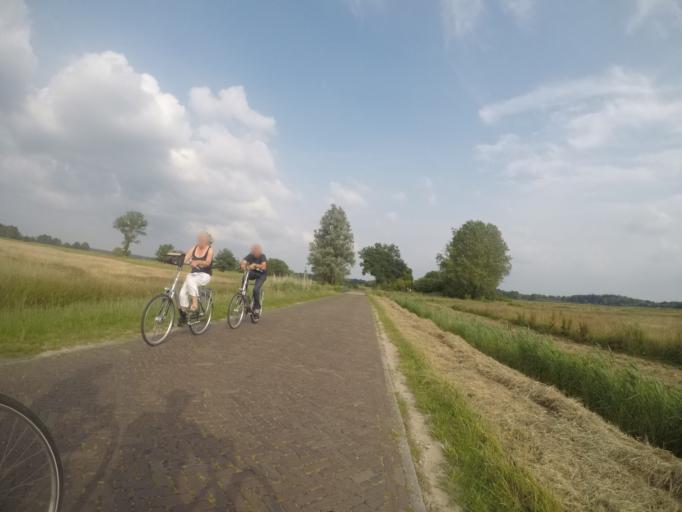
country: NL
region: Friesland
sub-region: Gemeente Weststellingwerf
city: Noordwolde
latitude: 52.8857
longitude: 6.2585
